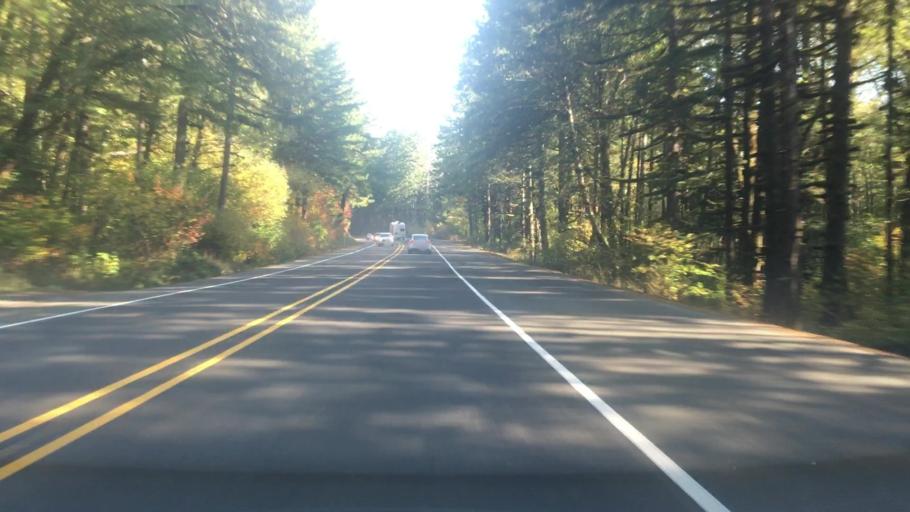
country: US
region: Oregon
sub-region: Lincoln County
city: Rose Lodge
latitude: 45.0558
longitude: -123.7519
